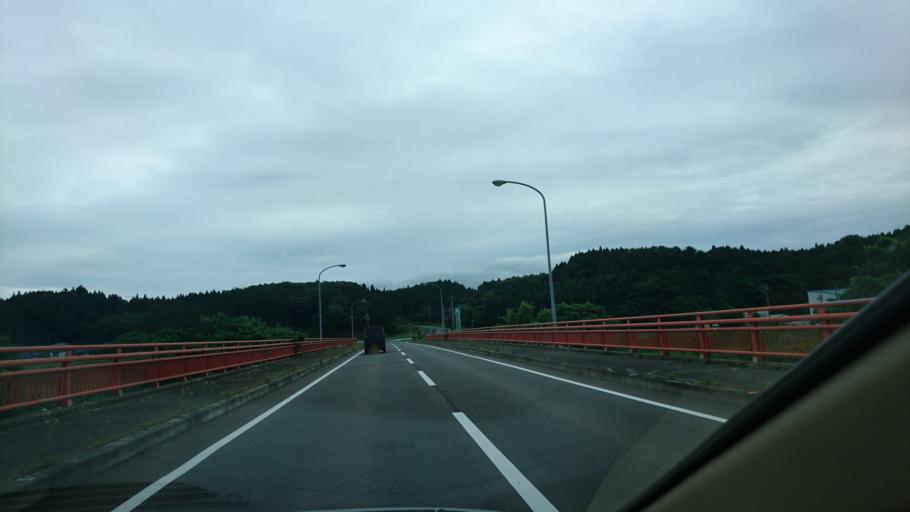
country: JP
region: Iwate
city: Mizusawa
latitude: 39.2109
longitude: 141.1625
